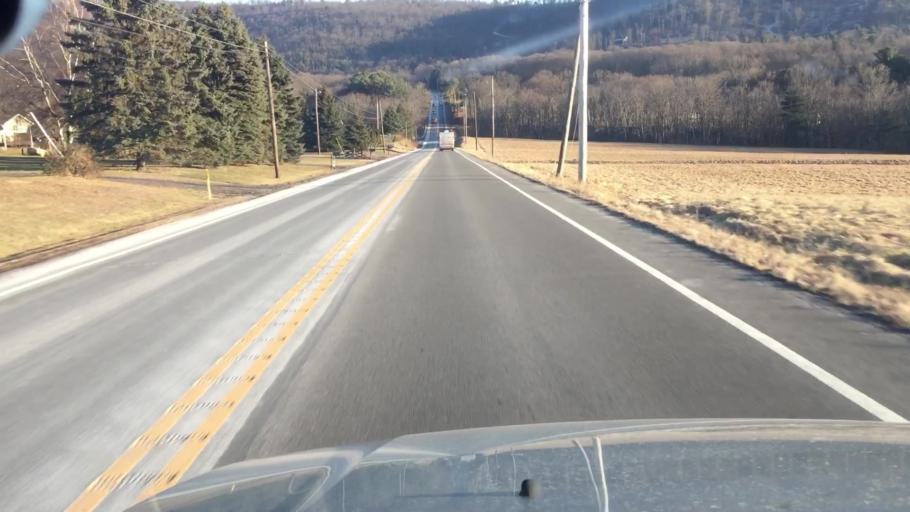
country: US
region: Pennsylvania
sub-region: Luzerne County
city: Nescopeck
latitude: 41.0392
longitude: -76.1382
